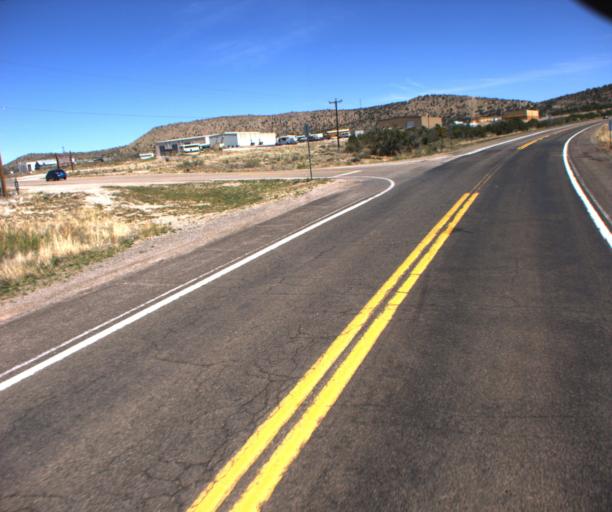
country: US
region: Arizona
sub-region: Mohave County
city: Peach Springs
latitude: 35.5400
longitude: -113.4159
